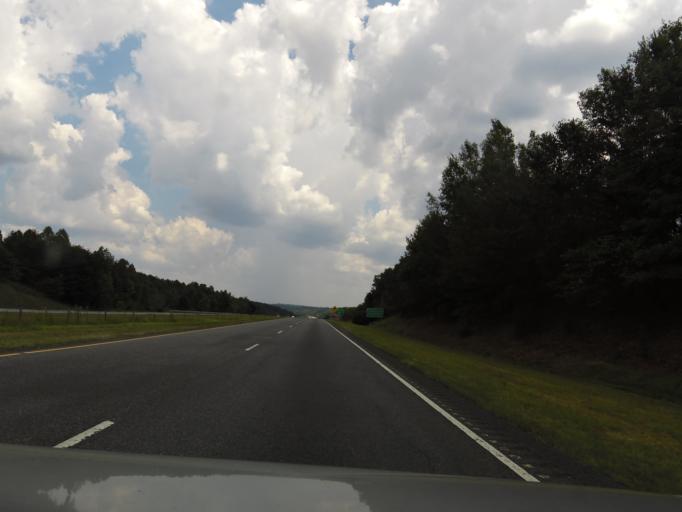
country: US
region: North Carolina
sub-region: Rutherford County
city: Rutherfordton
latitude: 35.2909
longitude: -82.0140
